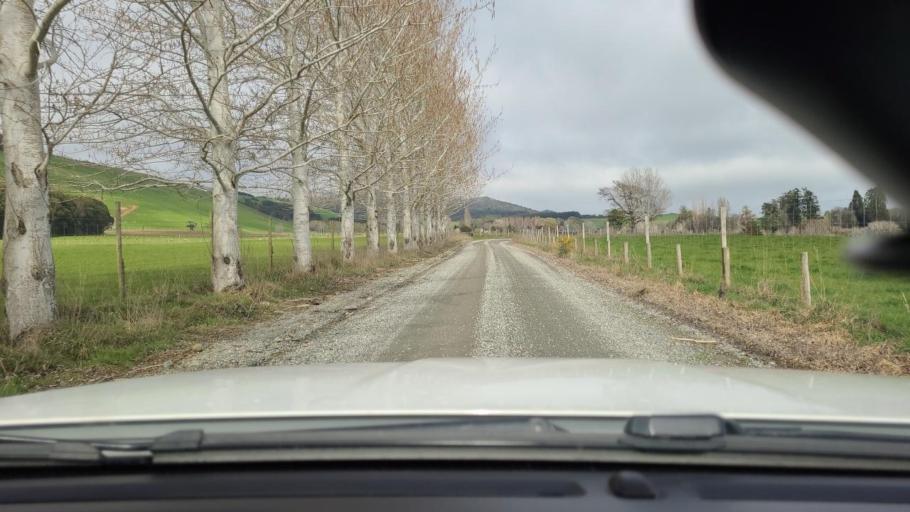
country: NZ
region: Southland
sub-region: Southland District
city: Riverton
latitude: -46.0785
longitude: 167.8498
